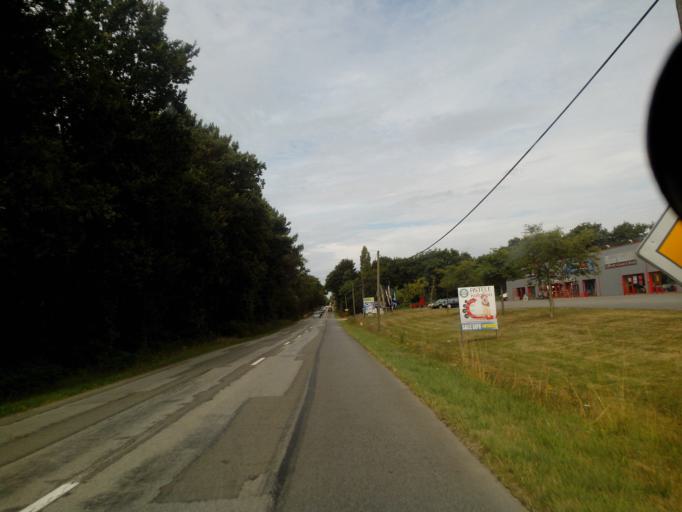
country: FR
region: Brittany
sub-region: Departement du Morbihan
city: Auray
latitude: 47.6660
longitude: -3.0283
